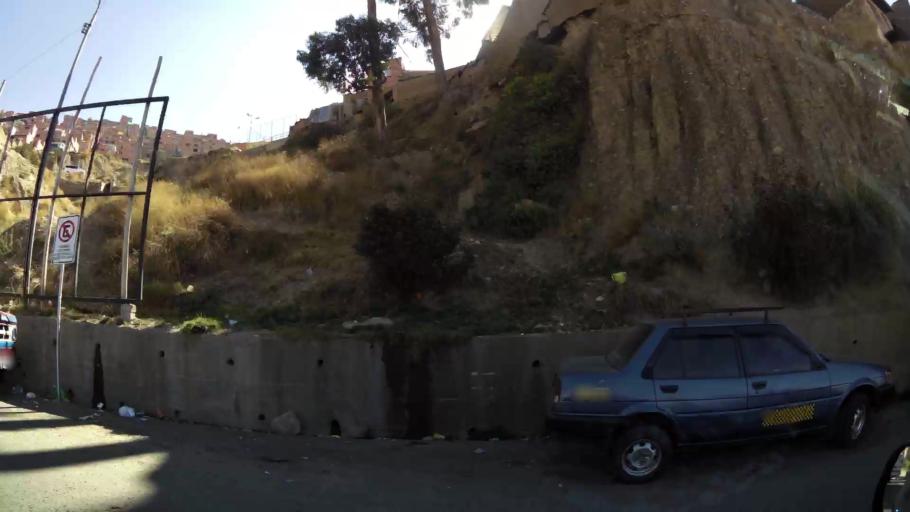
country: BO
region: La Paz
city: La Paz
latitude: -16.5139
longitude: -68.1486
